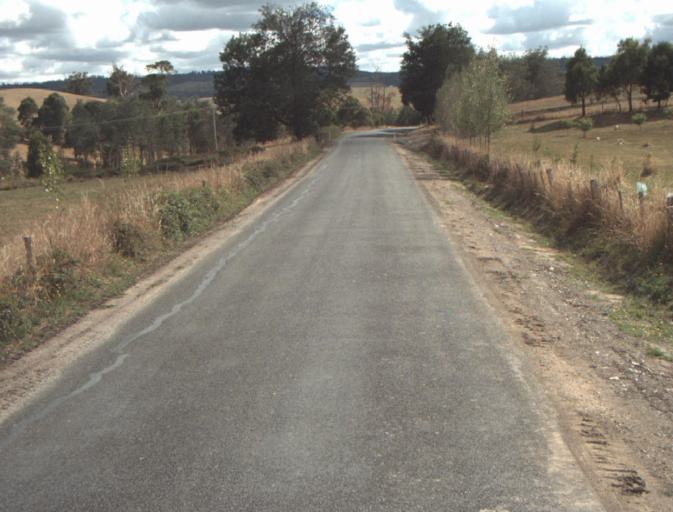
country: AU
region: Tasmania
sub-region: Launceston
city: Mayfield
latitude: -41.2587
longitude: 147.2078
